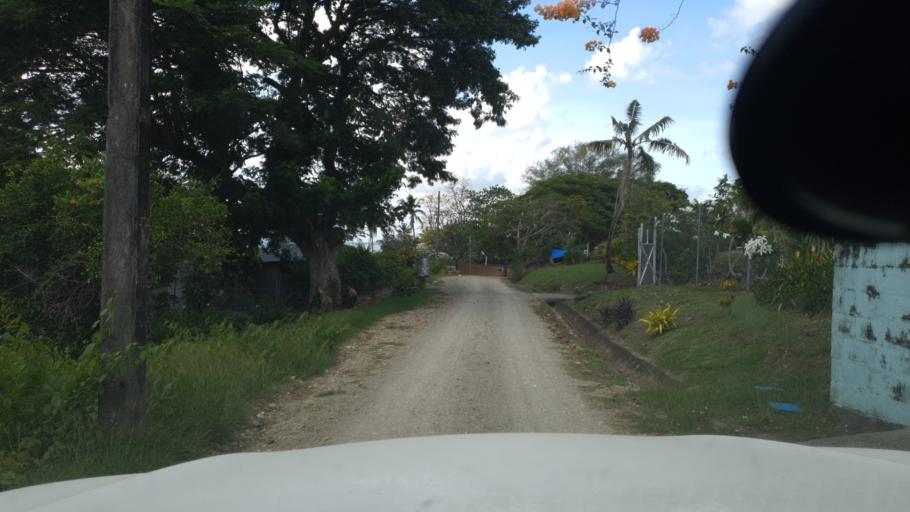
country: SB
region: Guadalcanal
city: Honiara
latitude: -9.4282
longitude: 159.9331
